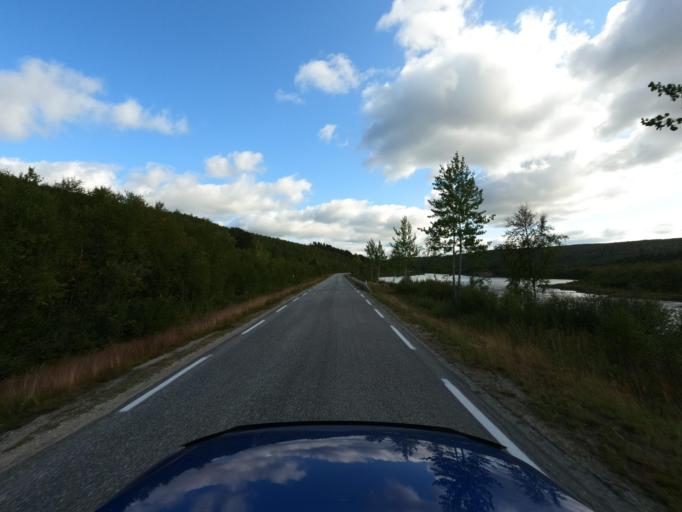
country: NO
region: Finnmark Fylke
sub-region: Porsanger
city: Lakselv
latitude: 69.4227
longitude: 24.8313
